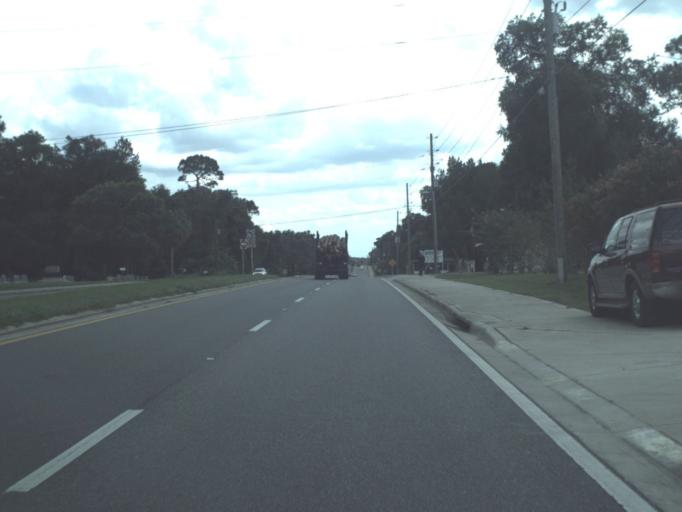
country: US
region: Florida
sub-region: Citrus County
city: Inverness Highlands South
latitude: 28.7946
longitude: -82.3051
